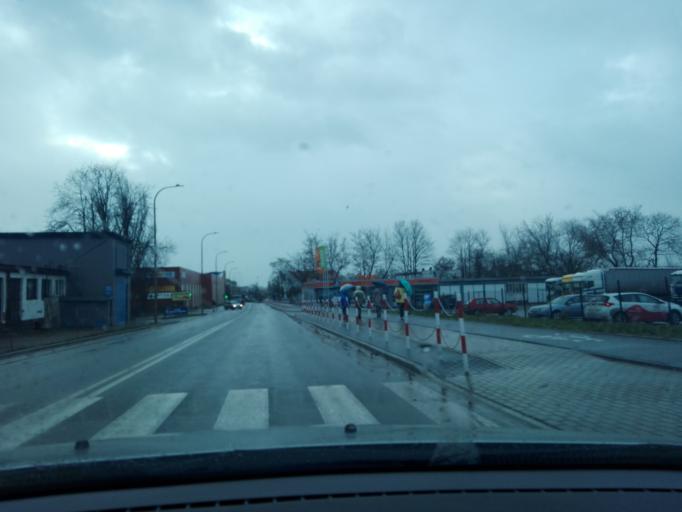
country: PL
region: Lodz Voivodeship
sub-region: Powiat kutnowski
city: Kutno
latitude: 52.2313
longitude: 19.3708
